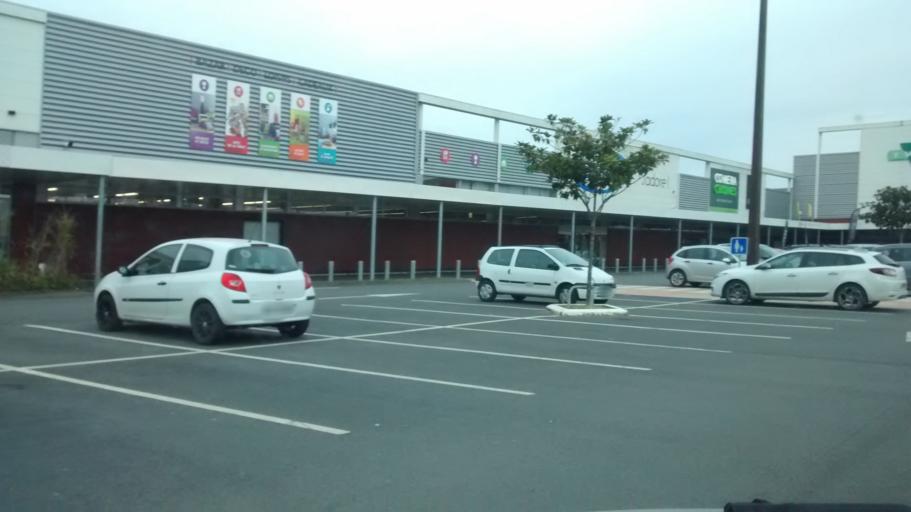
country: FR
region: Brittany
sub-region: Departement d'Ille-et-Vilaine
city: Liffre
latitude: 48.2249
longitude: -1.5006
